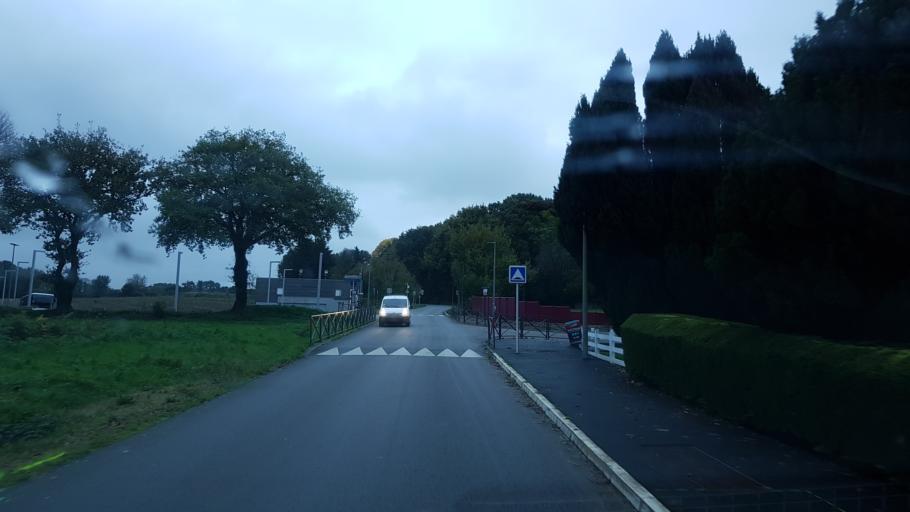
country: FR
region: Brittany
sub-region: Departement du Morbihan
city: Elven
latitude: 47.7247
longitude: -2.5876
